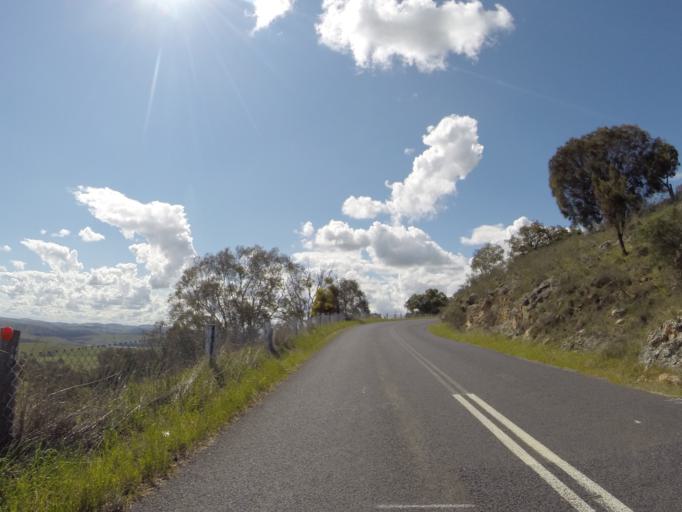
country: AU
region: New South Wales
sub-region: Yass Valley
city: Yass
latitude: -34.9867
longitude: 148.8410
